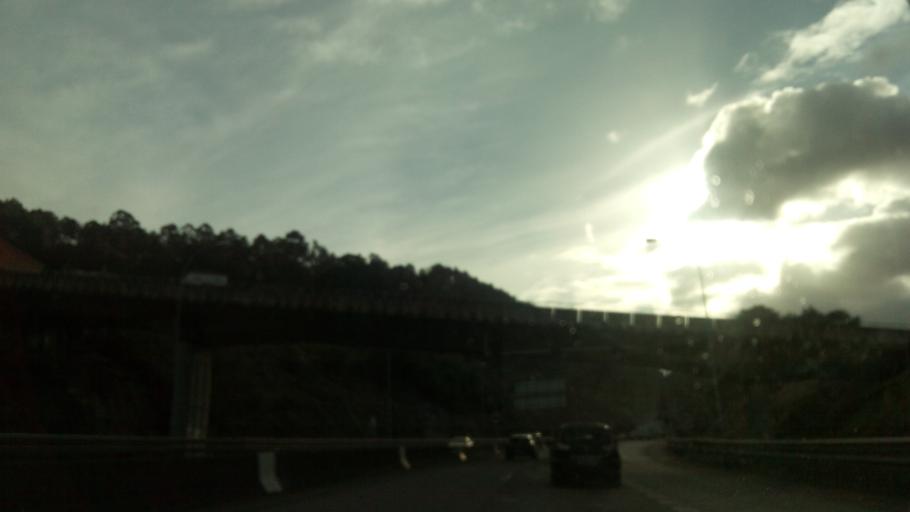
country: ES
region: Galicia
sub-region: Provincia de Pontevedra
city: Vigo
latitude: 42.2568
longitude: -8.6755
